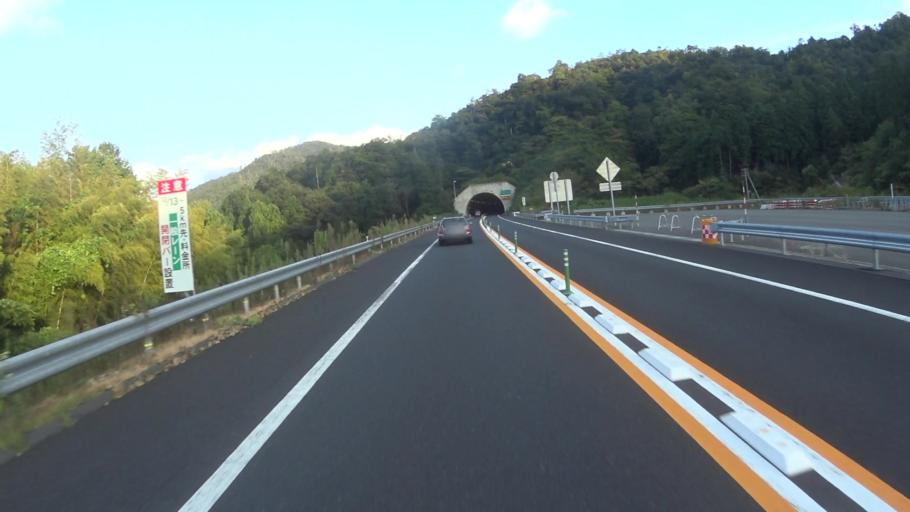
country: JP
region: Kyoto
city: Miyazu
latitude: 35.5480
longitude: 135.1488
